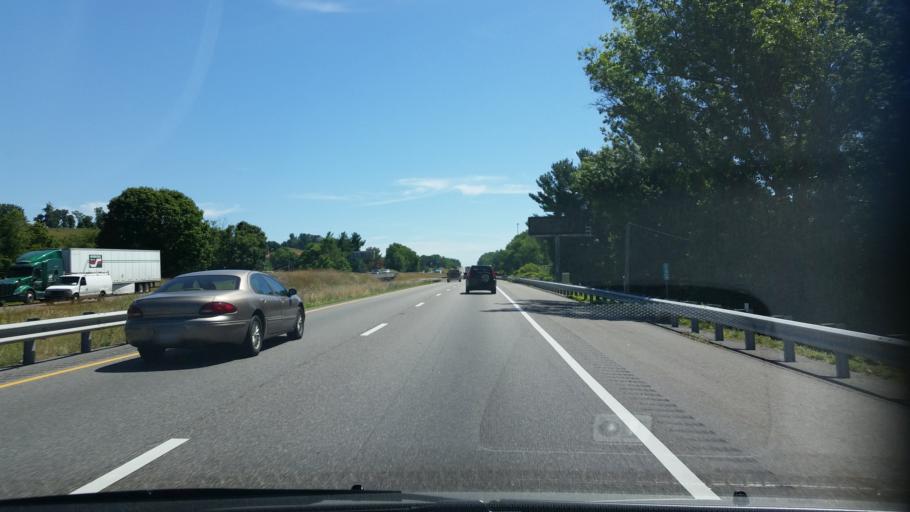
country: US
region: Virginia
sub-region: Washington County
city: Emory
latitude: 36.7569
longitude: -81.8590
